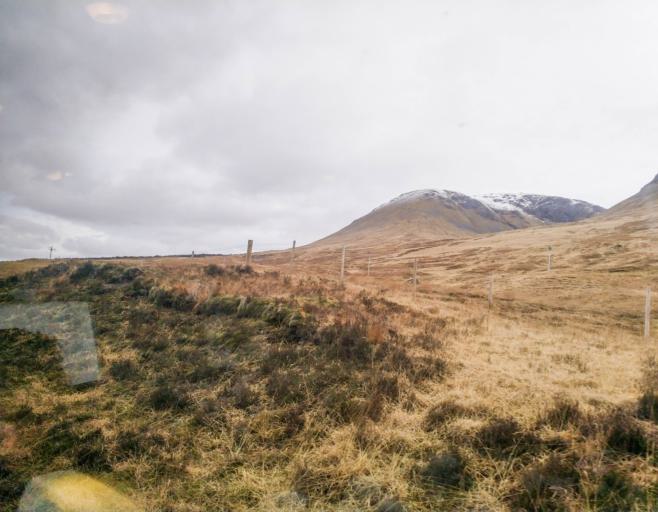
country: GB
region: Scotland
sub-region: Highland
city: Spean Bridge
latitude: 56.5108
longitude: -4.7604
